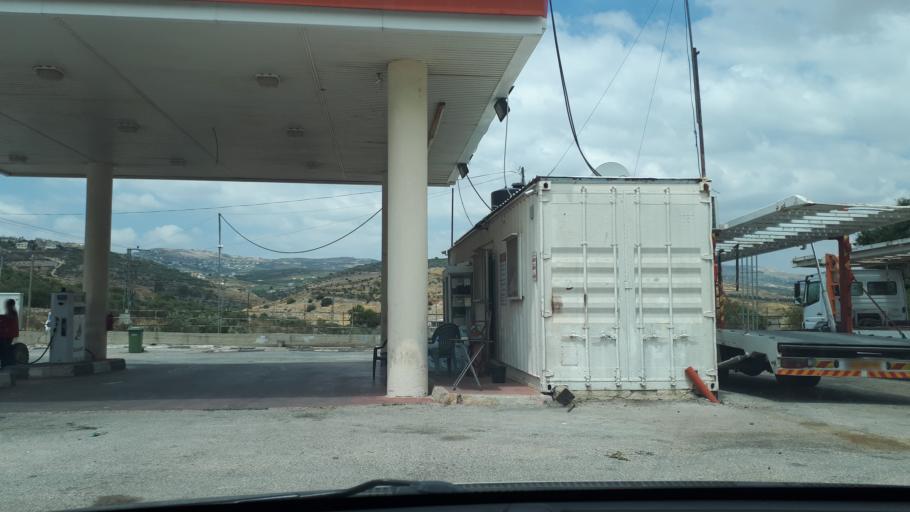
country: PS
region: West Bank
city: Ramin
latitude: 32.2717
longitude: 35.1458
